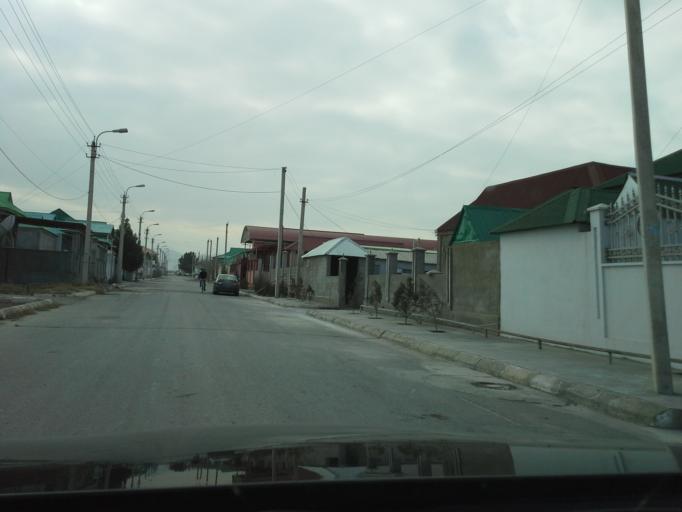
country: TM
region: Ahal
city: Abadan
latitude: 38.0422
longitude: 58.2713
